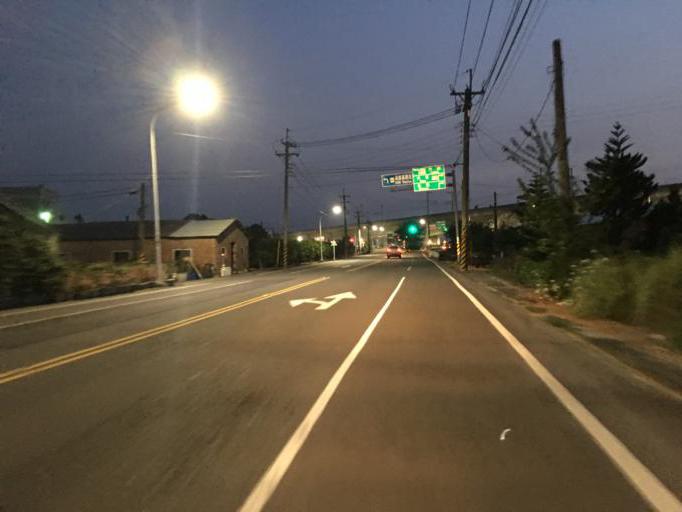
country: TW
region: Taiwan
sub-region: Chiayi
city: Taibao
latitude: 23.5343
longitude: 120.3287
